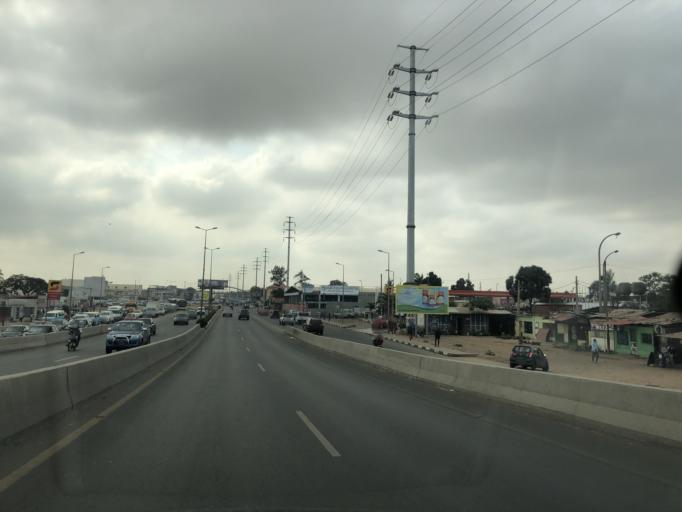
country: AO
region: Luanda
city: Luanda
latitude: -8.8352
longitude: 13.2571
